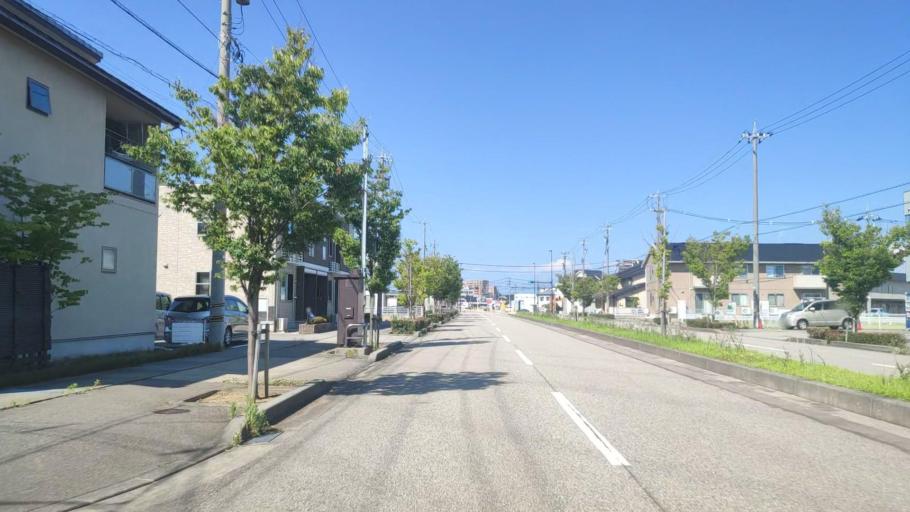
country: JP
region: Ishikawa
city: Kanazawa-shi
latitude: 36.5789
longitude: 136.6295
